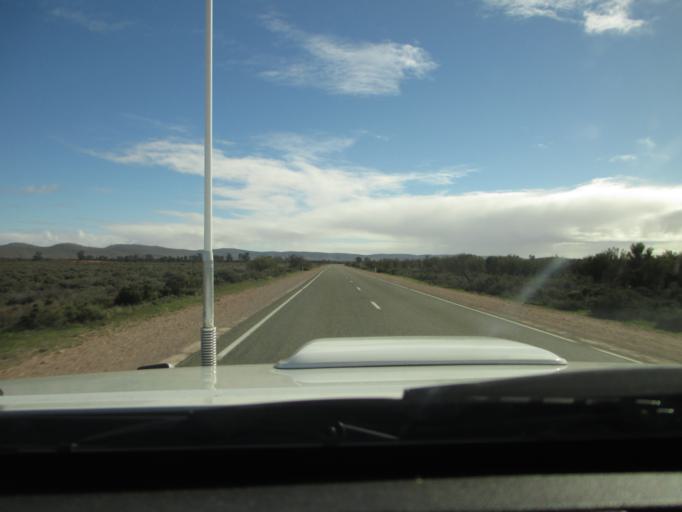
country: AU
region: South Australia
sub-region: Flinders Ranges
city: Quorn
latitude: -31.7725
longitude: 138.3354
